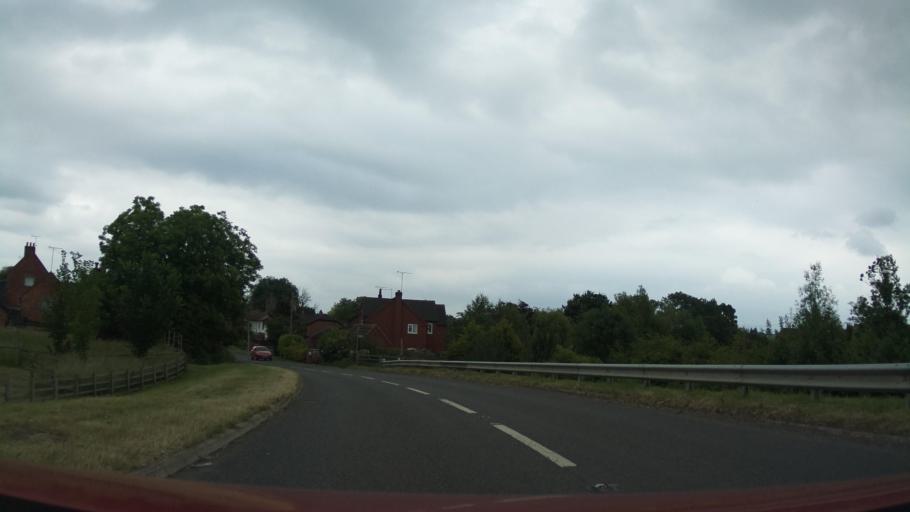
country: GB
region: England
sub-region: Derbyshire
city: Rodsley
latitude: 52.8697
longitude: -1.7191
